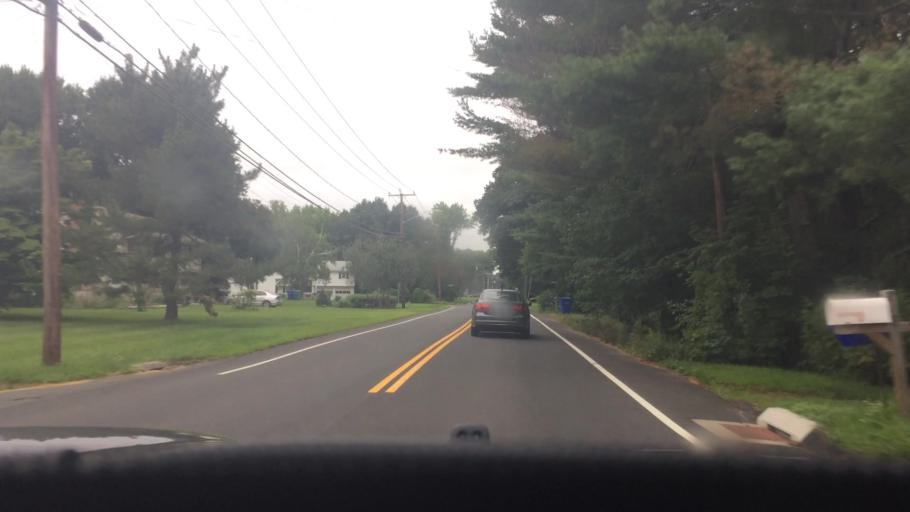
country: US
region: Connecticut
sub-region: Hartford County
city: Blue Hills
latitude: 41.8530
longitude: -72.7311
